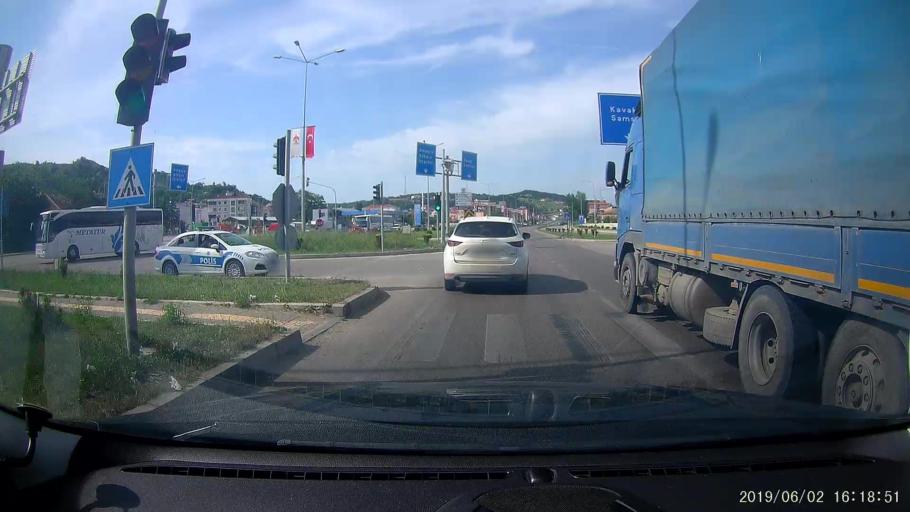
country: TR
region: Samsun
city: Havza
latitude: 40.9615
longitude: 35.6661
